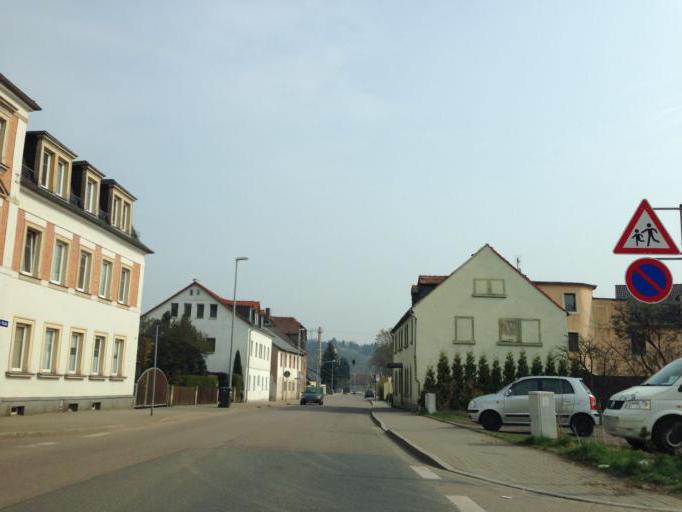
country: DE
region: Saxony
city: Freital
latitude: 51.0127
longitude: 13.6686
